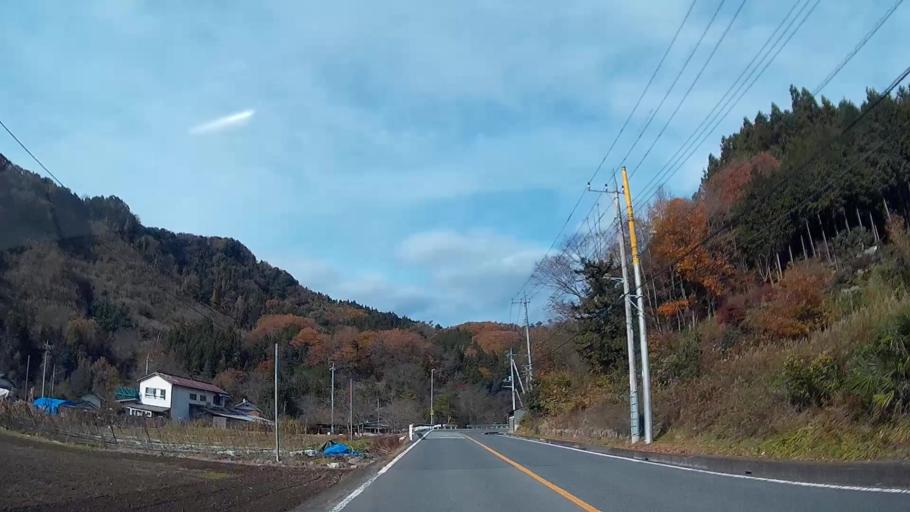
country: JP
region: Saitama
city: Chichibu
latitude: 36.0482
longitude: 138.9832
